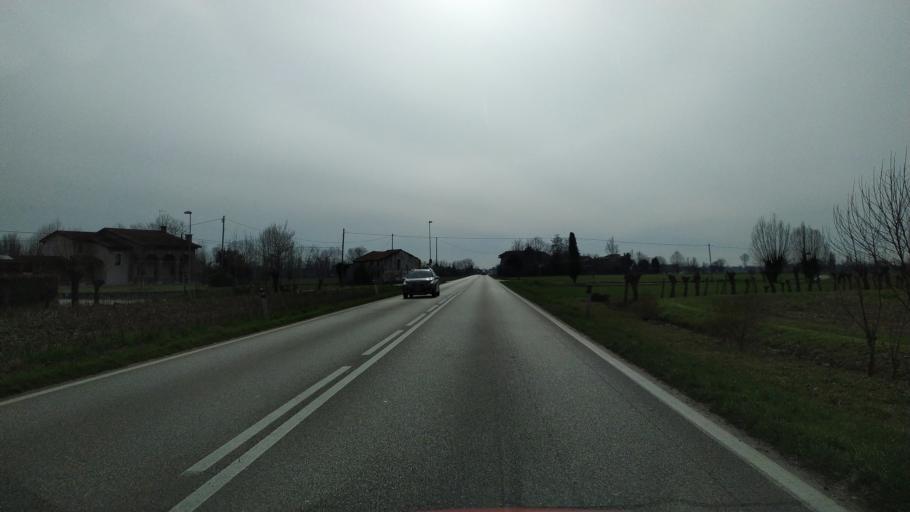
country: IT
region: Veneto
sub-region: Provincia di Padova
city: Grantorto
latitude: 45.5931
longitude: 11.7253
